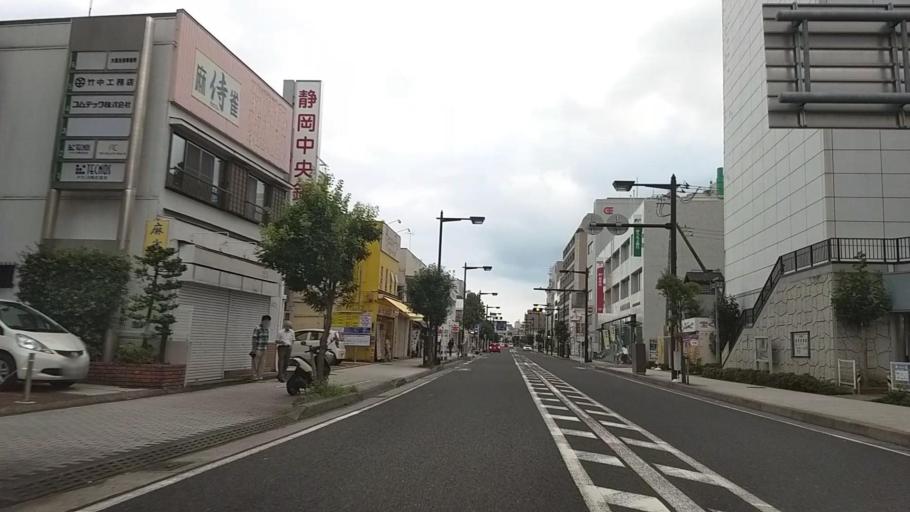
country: JP
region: Kanagawa
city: Odawara
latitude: 35.2532
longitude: 139.1593
